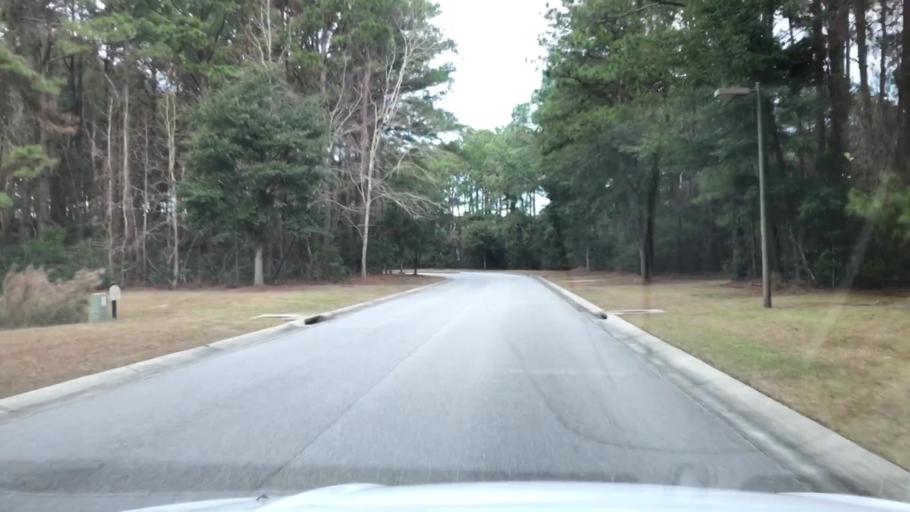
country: US
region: South Carolina
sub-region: Charleston County
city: Isle of Palms
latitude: 32.9079
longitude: -79.7219
